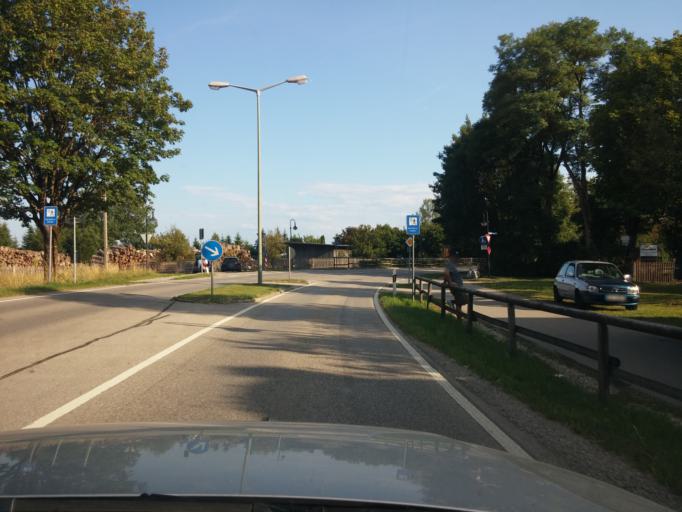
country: DE
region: Bavaria
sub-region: Upper Bavaria
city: Hohenbrunn
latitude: 48.0494
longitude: 11.7055
